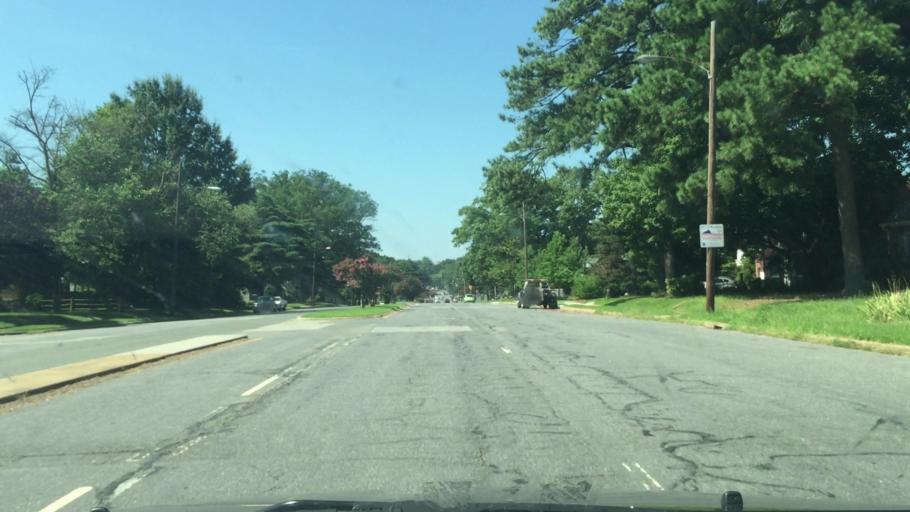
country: US
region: Virginia
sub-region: Henrico County
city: Dumbarton
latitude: 37.5817
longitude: -77.5121
